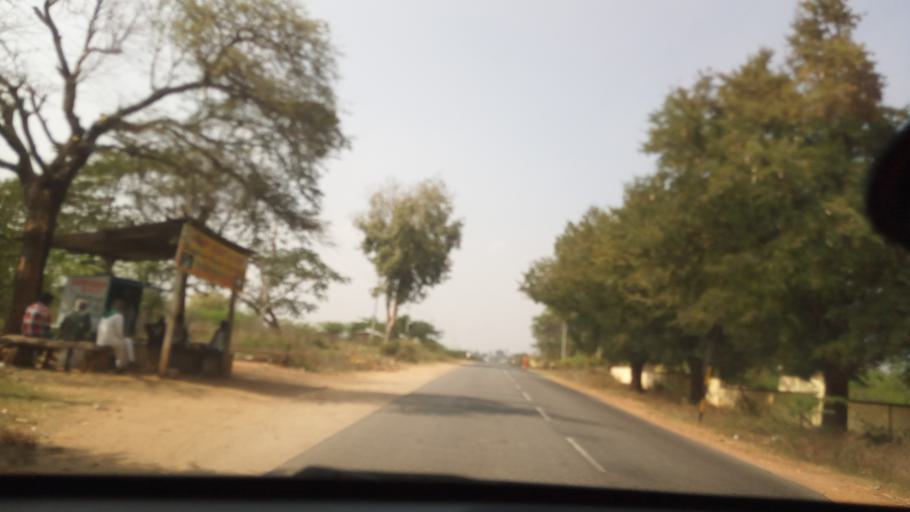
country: IN
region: Karnataka
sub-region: Mysore
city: Nanjangud
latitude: 12.0852
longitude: 76.7310
